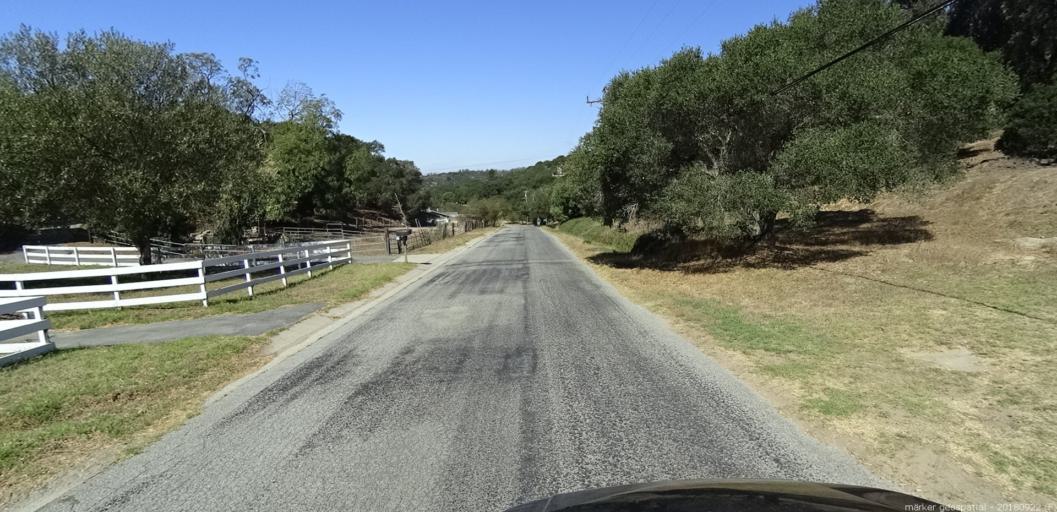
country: US
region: California
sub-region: Monterey County
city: Prunedale
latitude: 36.8100
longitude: -121.6313
